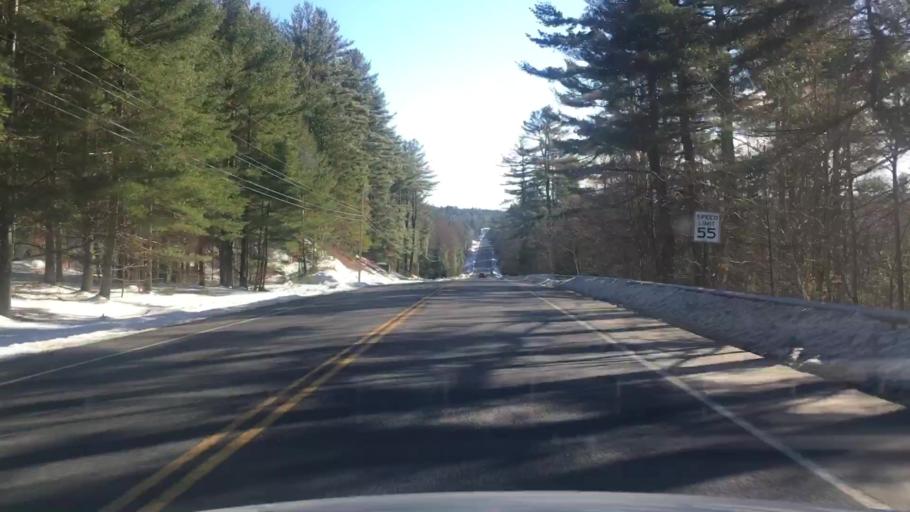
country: US
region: Maine
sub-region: Somerset County
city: Madison
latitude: 44.9334
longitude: -69.8369
